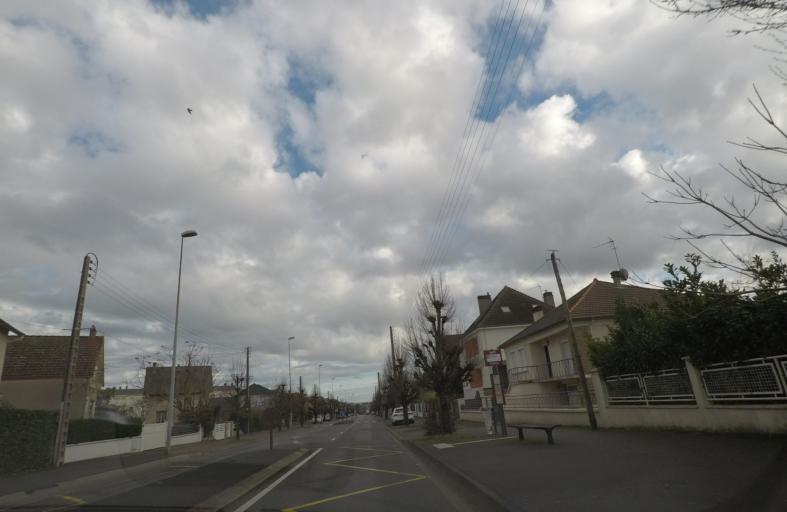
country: FR
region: Centre
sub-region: Departement du Cher
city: Bourges
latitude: 47.0698
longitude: 2.3781
